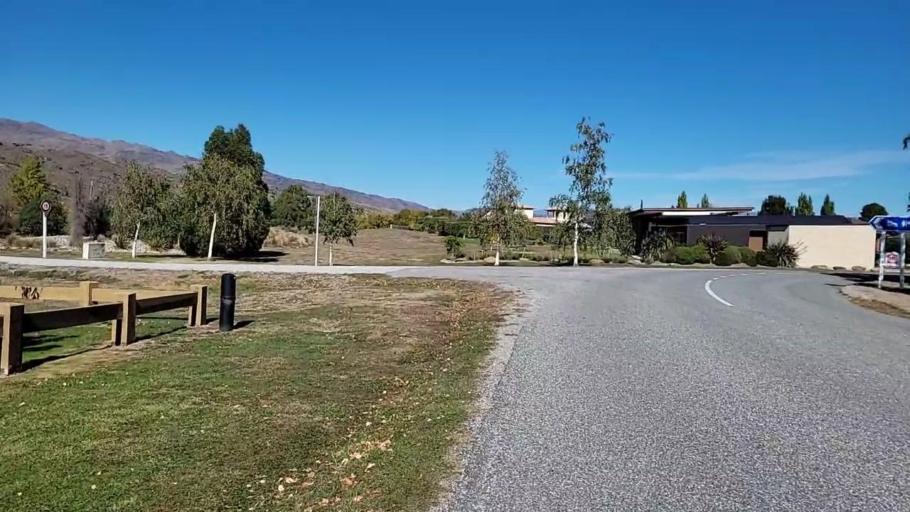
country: NZ
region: Otago
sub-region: Queenstown-Lakes District
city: Wanaka
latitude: -44.9733
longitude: 169.2461
